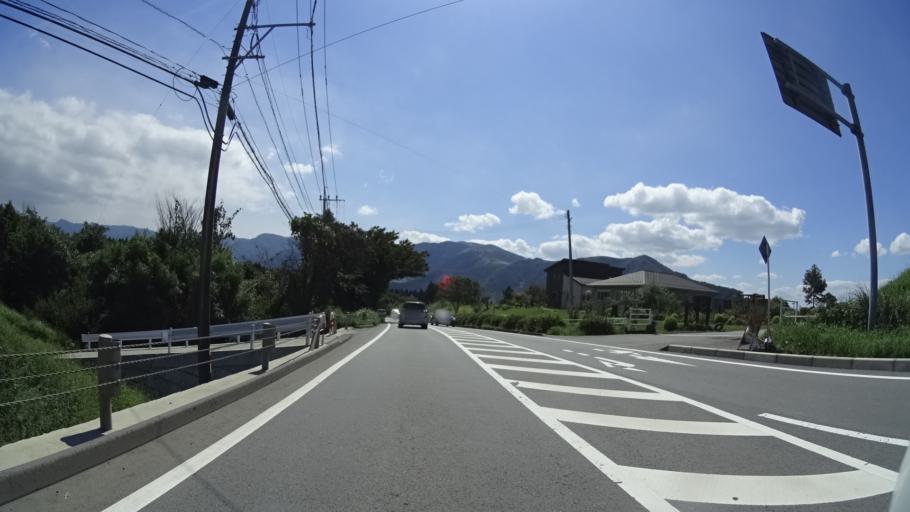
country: JP
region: Kumamoto
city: Aso
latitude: 32.8758
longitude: 131.0050
